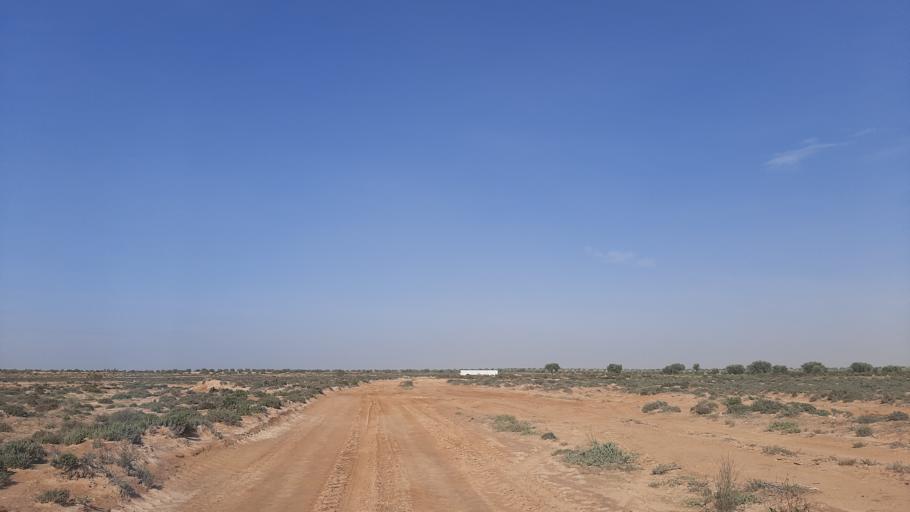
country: TN
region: Madanin
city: Zarzis
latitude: 33.4480
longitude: 10.8078
